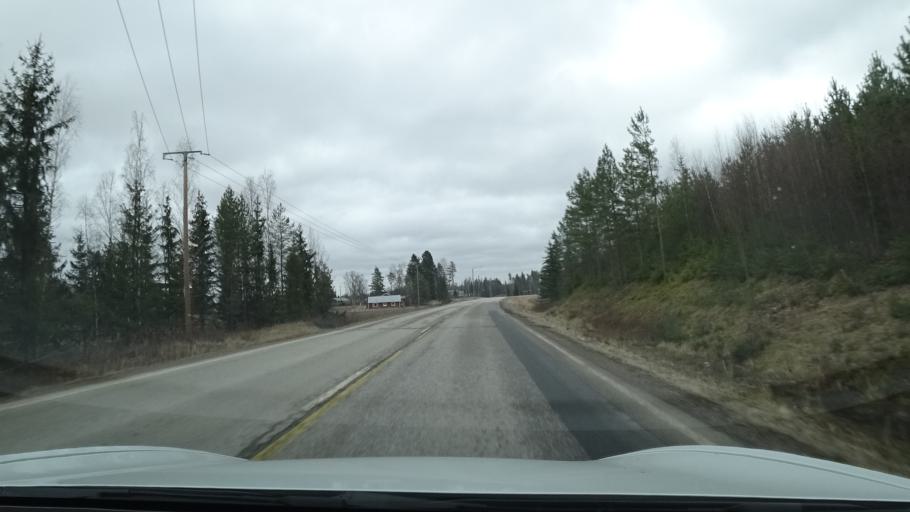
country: FI
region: Uusimaa
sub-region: Porvoo
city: Pukkila
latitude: 60.6525
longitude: 25.6665
